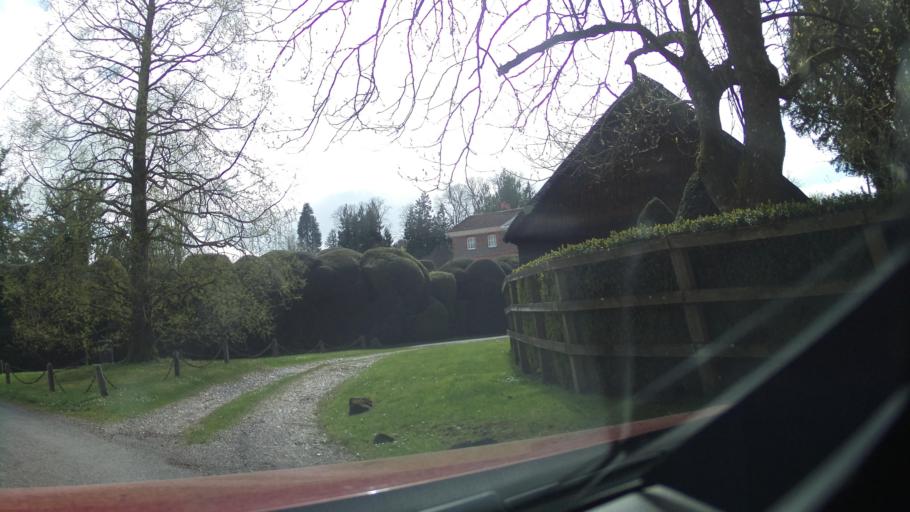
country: GB
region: England
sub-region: West Berkshire
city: Kintbury
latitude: 51.3185
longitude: -1.4608
